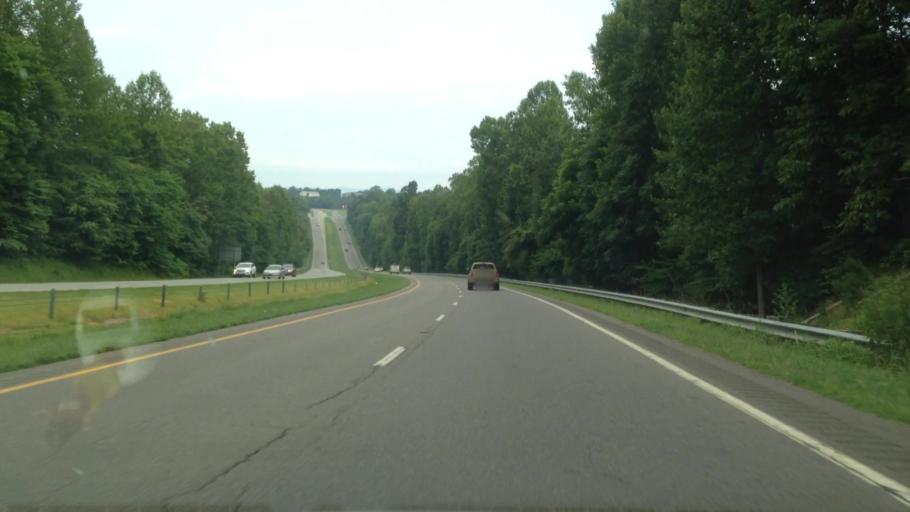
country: US
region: North Carolina
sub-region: Surry County
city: Flat Rock
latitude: 36.4633
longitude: -80.5637
